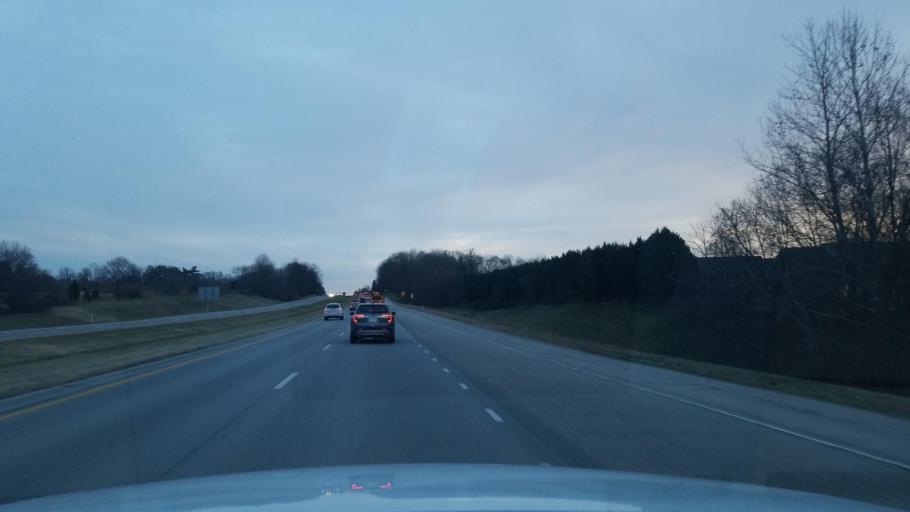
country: US
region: Indiana
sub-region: Vanderburgh County
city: Evansville
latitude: 37.9679
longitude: -87.6720
